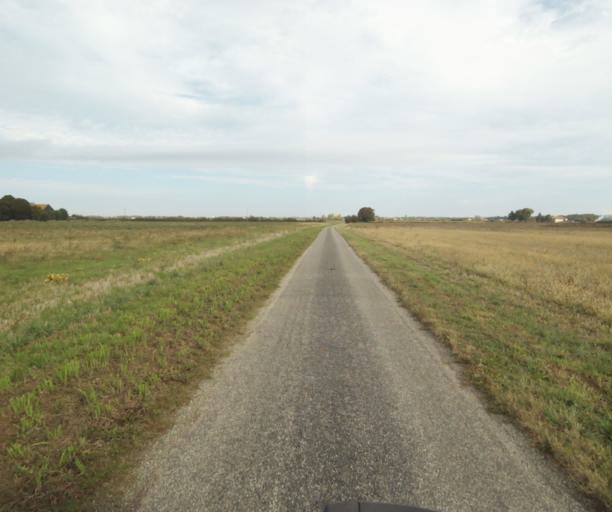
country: FR
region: Midi-Pyrenees
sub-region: Departement du Tarn-et-Garonne
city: Finhan
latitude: 43.9284
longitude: 1.2247
